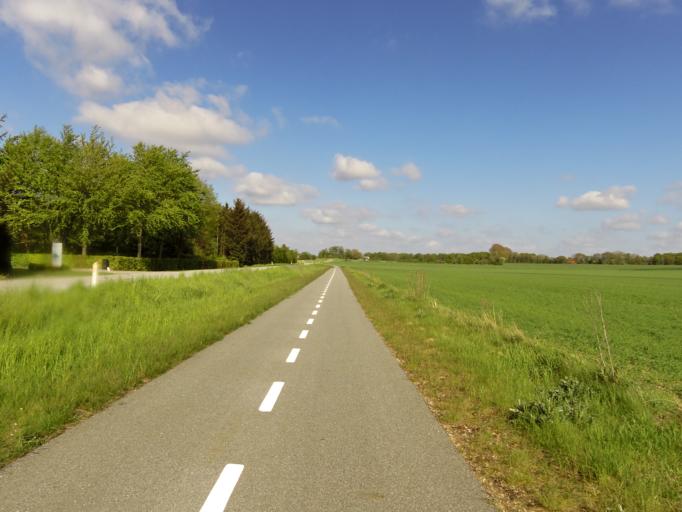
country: DK
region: South Denmark
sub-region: Vejen Kommune
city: Rodding
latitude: 55.3638
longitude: 9.0386
